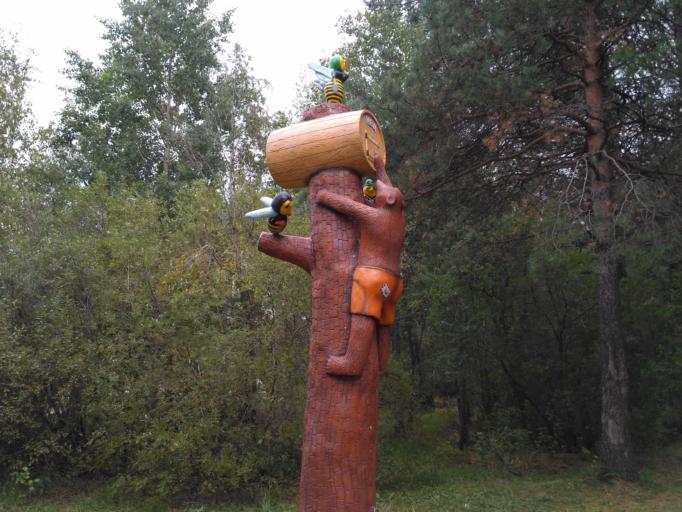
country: RU
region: Khanty-Mansiyskiy Avtonomnyy Okrug
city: Surgut
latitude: 61.2423
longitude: 73.4159
